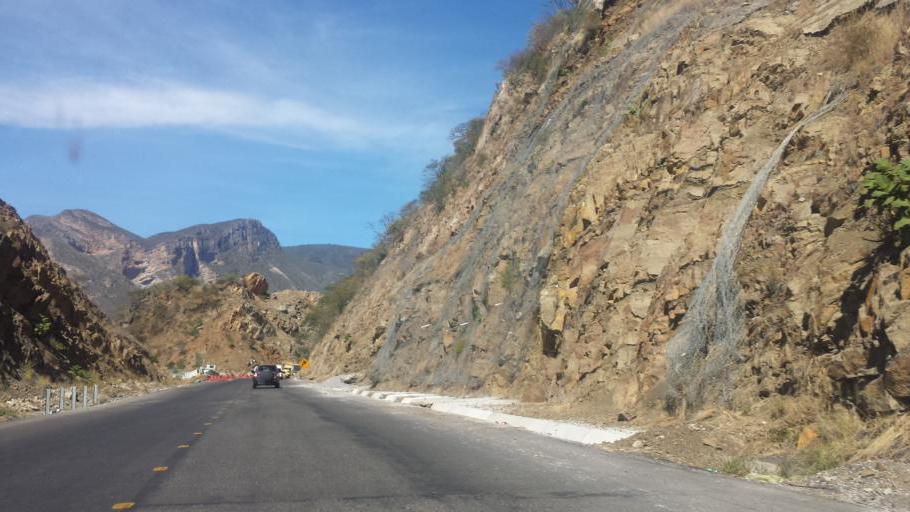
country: MX
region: Puebla
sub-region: San Jose Miahuatlan
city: San Pedro Tetitlan
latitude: 18.1140
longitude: -97.3398
